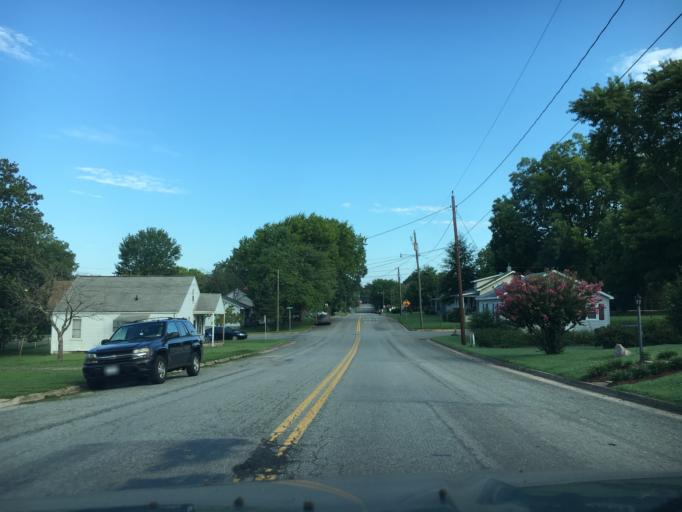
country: US
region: Virginia
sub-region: Halifax County
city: South Boston
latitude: 36.7001
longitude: -78.9079
